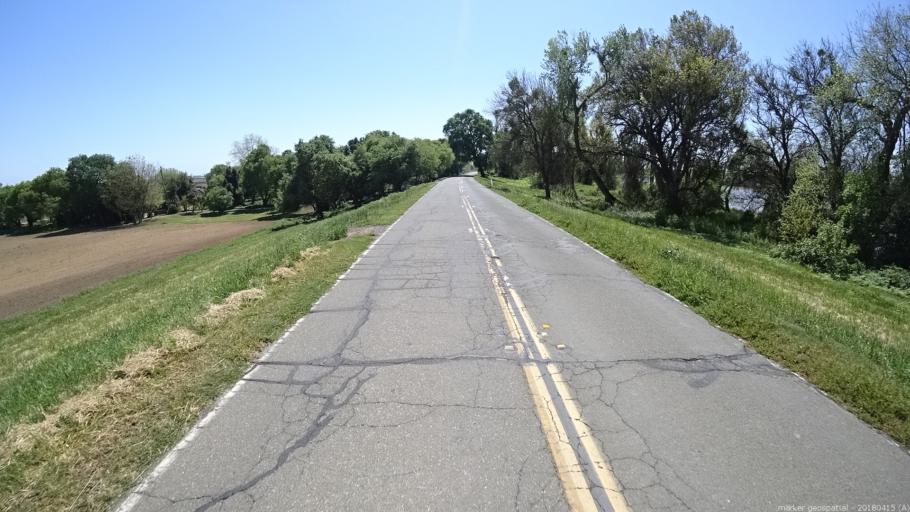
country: US
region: California
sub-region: Sacramento County
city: Walnut Grove
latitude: 38.2343
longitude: -121.6016
